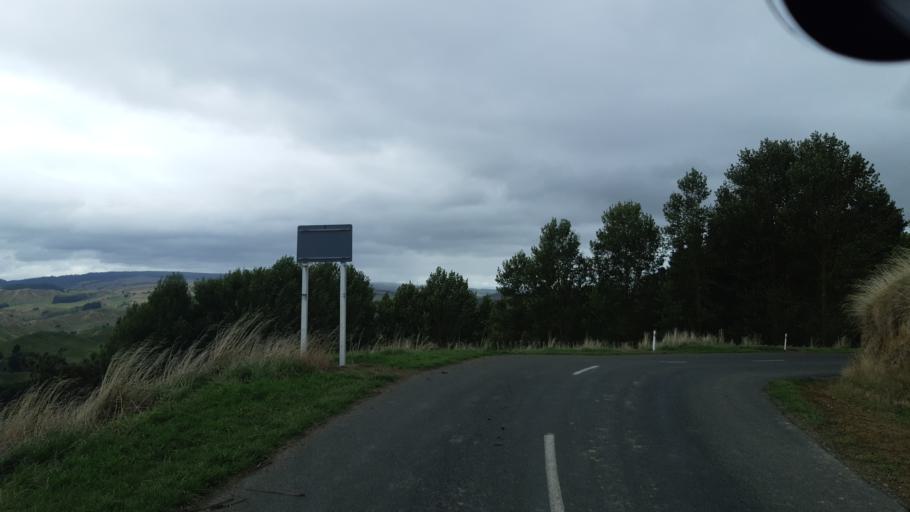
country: NZ
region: Manawatu-Wanganui
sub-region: Ruapehu District
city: Waiouru
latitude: -39.6109
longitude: 175.6576
